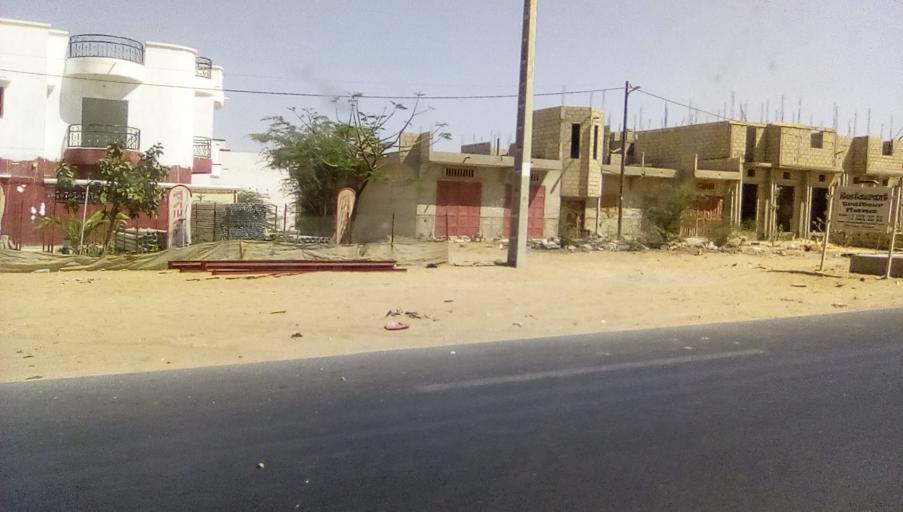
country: SN
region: Saint-Louis
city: Saint-Louis
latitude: 16.0425
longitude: -16.4405
